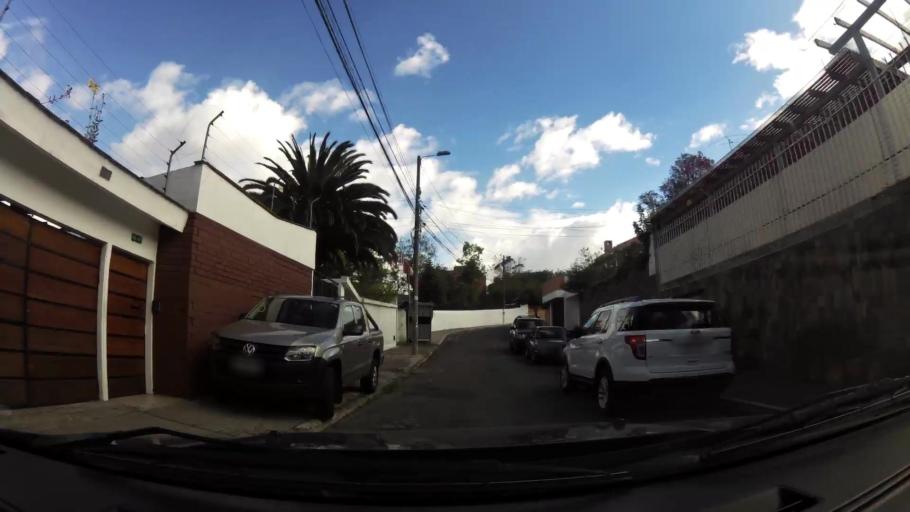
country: EC
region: Pichincha
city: Quito
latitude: -0.2065
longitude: -78.4802
